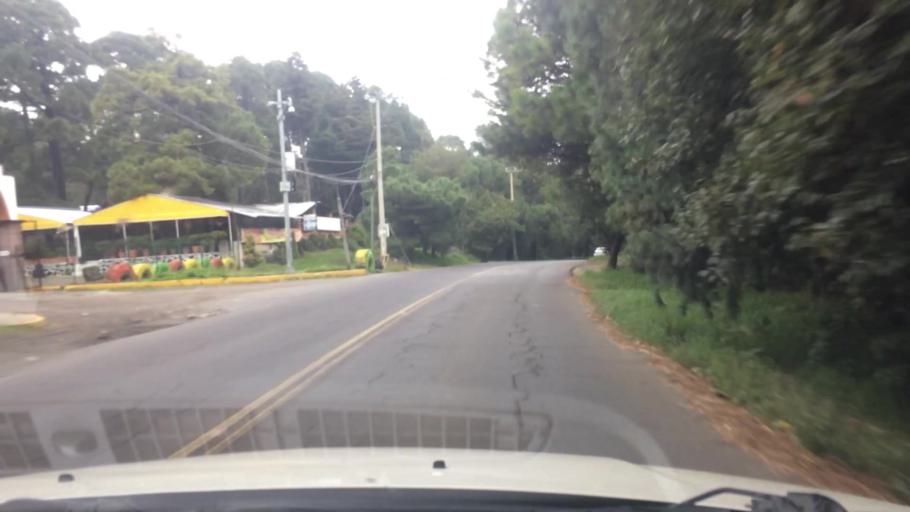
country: MX
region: Mexico City
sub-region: Tlalpan
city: Lomas de Tepemecatl
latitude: 19.2533
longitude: -99.2446
